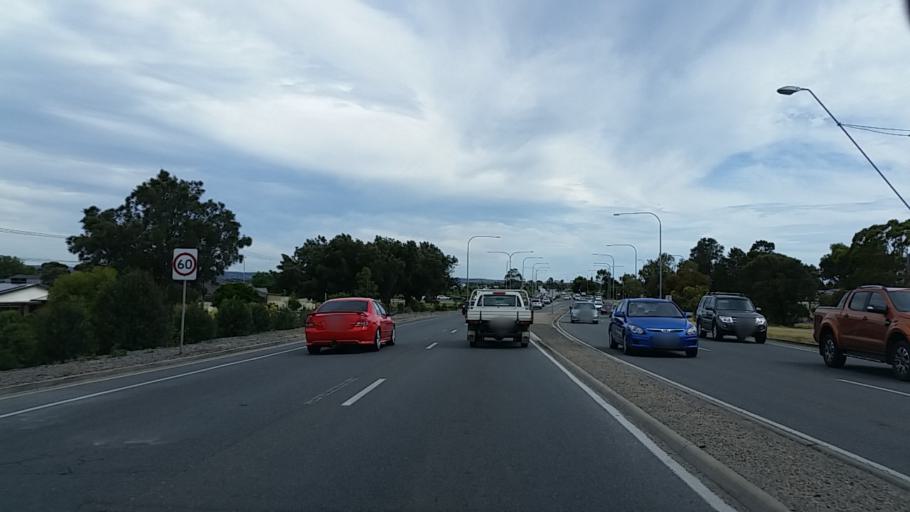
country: AU
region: South Australia
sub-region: Charles Sturt
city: Henley Beach
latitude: -34.9323
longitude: 138.5176
